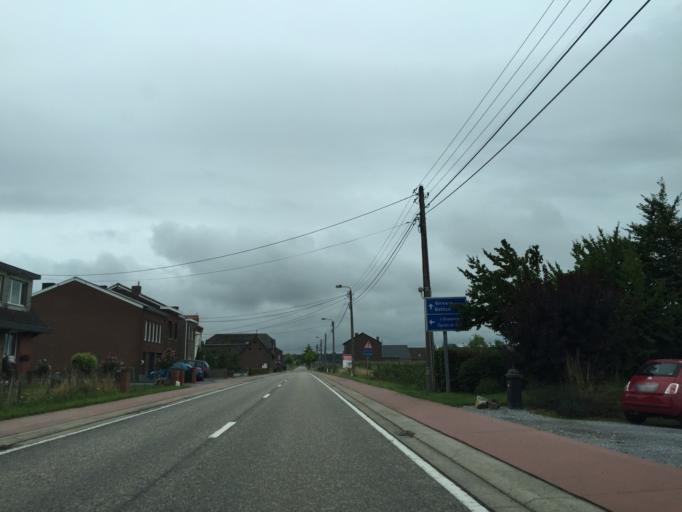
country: NL
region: Limburg
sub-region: Eijsden-Margraten
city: Eijsden
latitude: 50.7591
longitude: 5.7239
